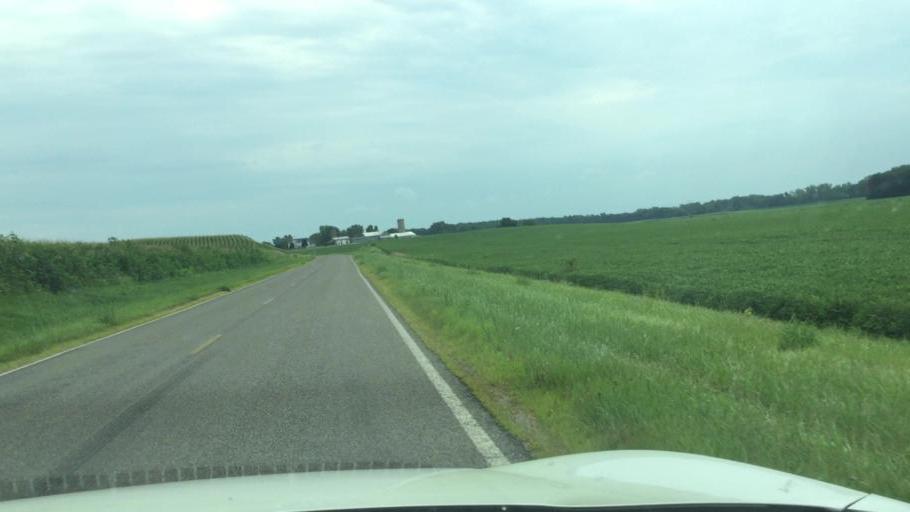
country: US
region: Ohio
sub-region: Champaign County
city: Mechanicsburg
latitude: 40.0637
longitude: -83.6520
